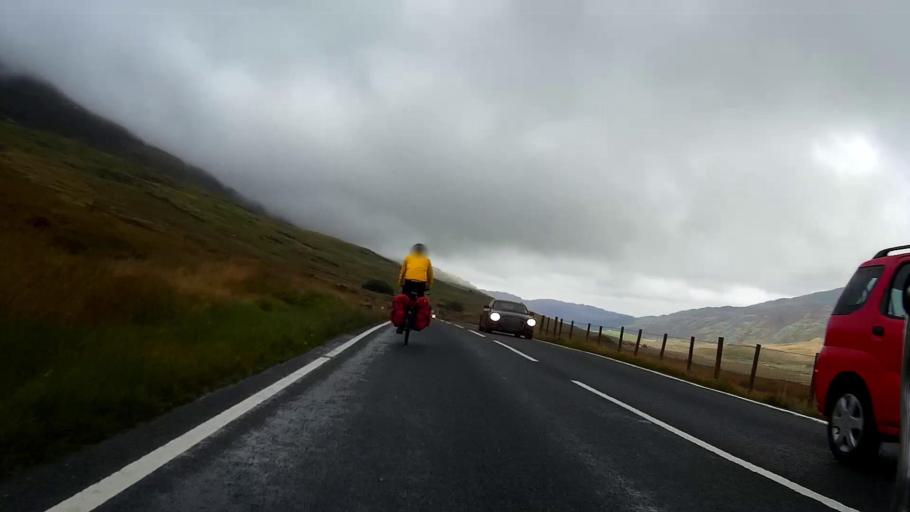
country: GB
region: Wales
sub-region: Gwynedd
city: Blaenau-Ffestiniog
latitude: 53.0864
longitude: -3.9880
